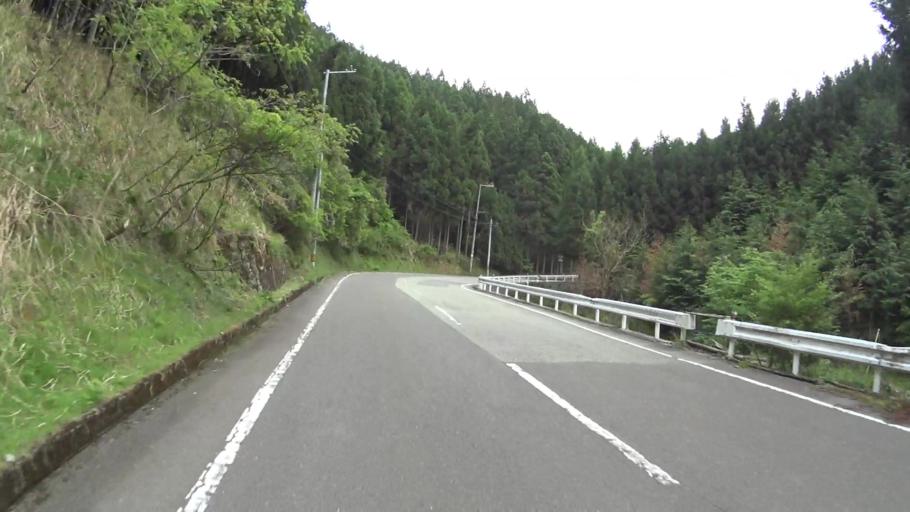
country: JP
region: Kyoto
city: Kameoka
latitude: 35.1350
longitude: 135.6174
